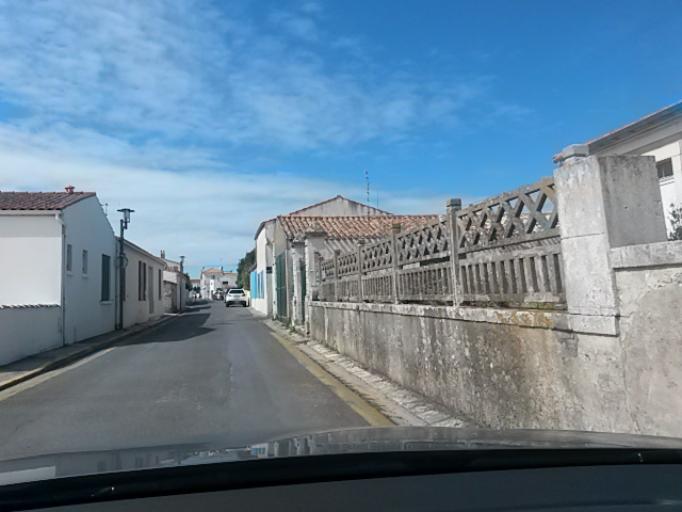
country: FR
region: Poitou-Charentes
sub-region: Departement de la Charente-Maritime
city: Dolus-d'Oleron
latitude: 45.9179
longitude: -1.3323
